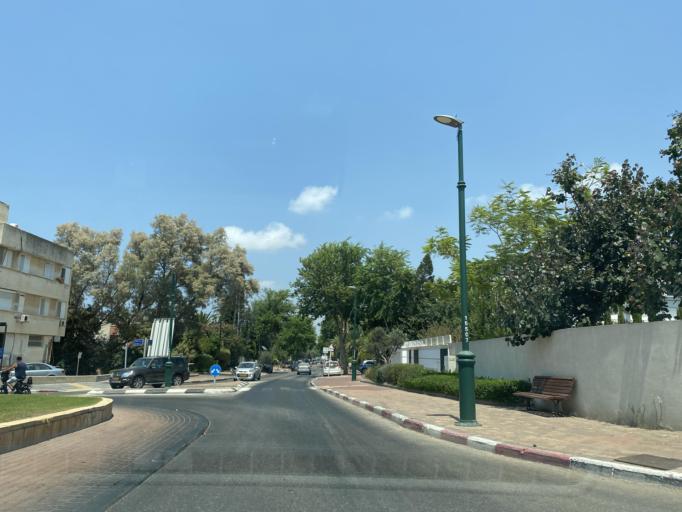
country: IL
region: Tel Aviv
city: Herzliya Pituah
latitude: 32.1790
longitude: 34.8060
